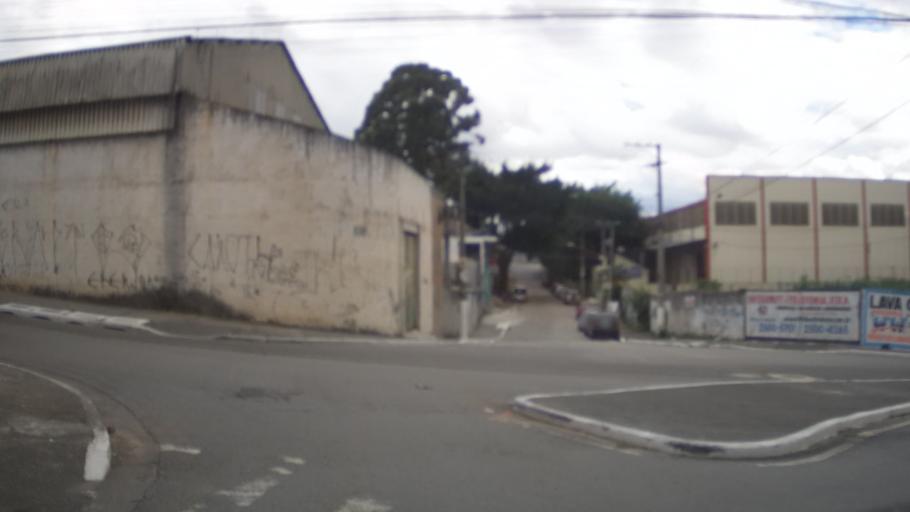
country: BR
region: Sao Paulo
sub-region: Guarulhos
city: Guarulhos
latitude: -23.4854
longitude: -46.5567
